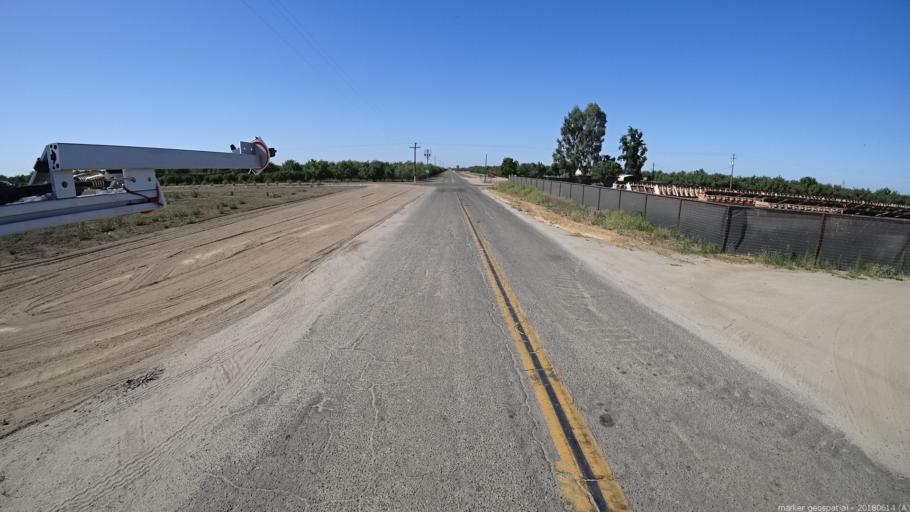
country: US
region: California
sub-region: Madera County
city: Fairmead
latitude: 36.9971
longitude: -120.1661
